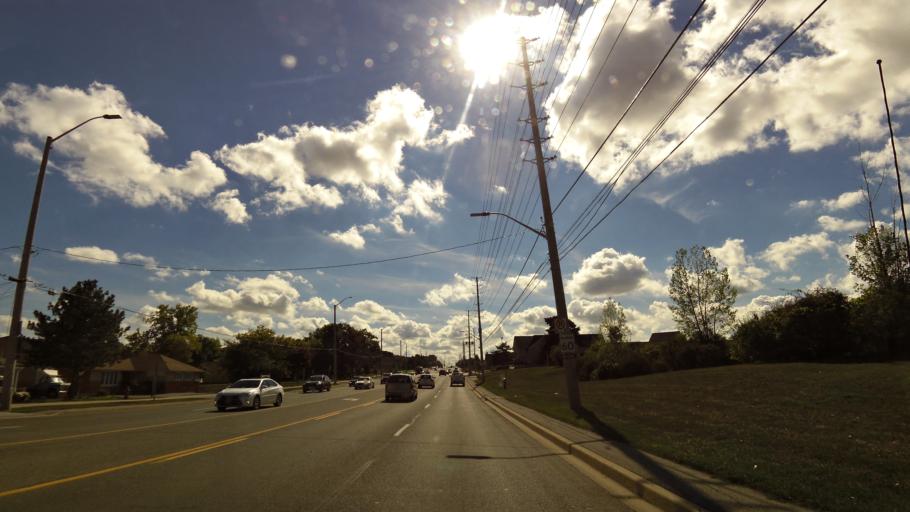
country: CA
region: Ontario
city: Mississauga
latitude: 43.5840
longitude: -79.7273
